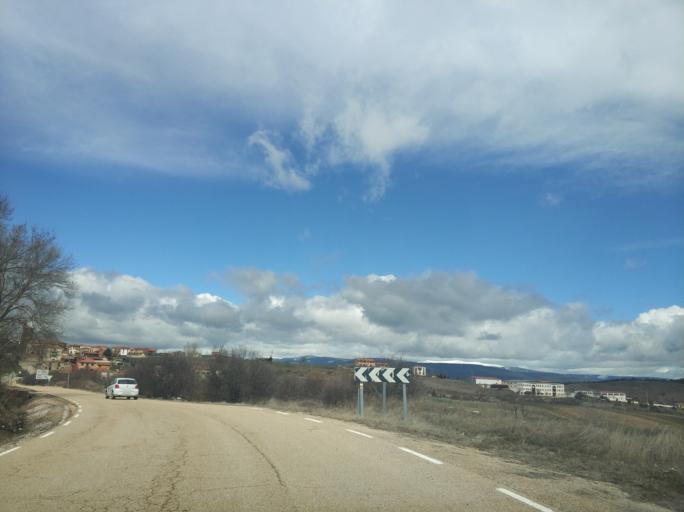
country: ES
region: Castille and Leon
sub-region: Provincia de Soria
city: Abejar
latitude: 41.8040
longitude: -2.7810
